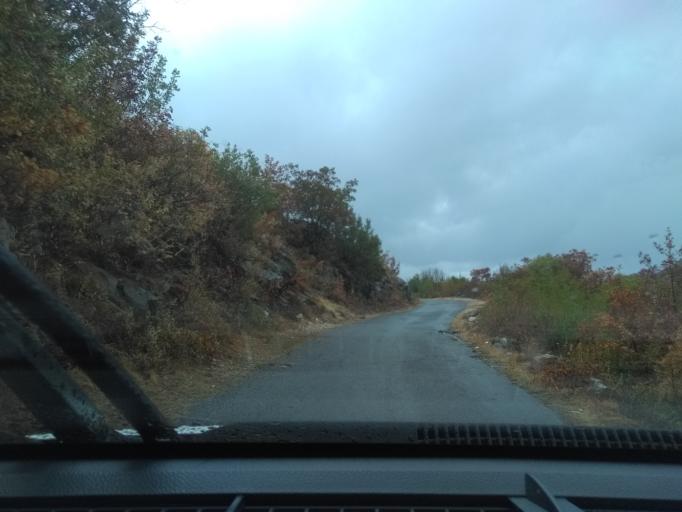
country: ME
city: Stari Bar
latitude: 42.1855
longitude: 19.1729
